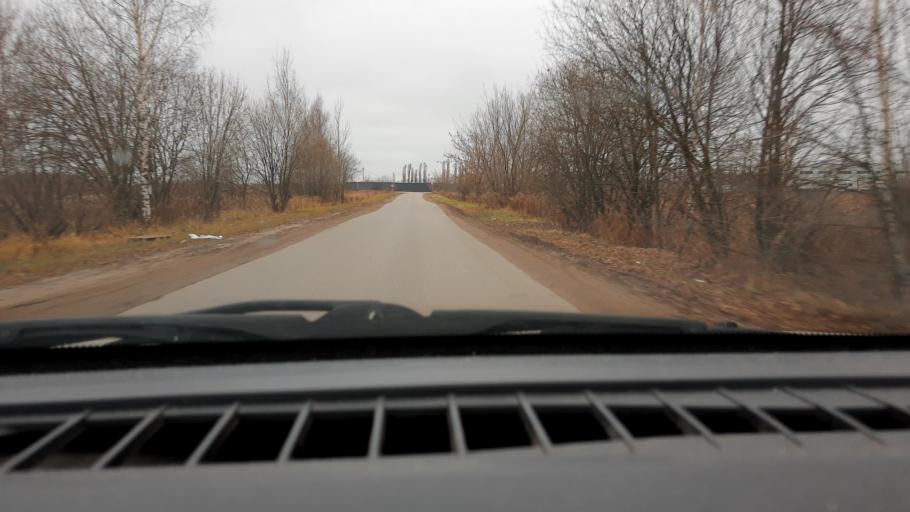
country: RU
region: Nizjnij Novgorod
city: Kstovo
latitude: 56.1958
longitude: 44.1377
